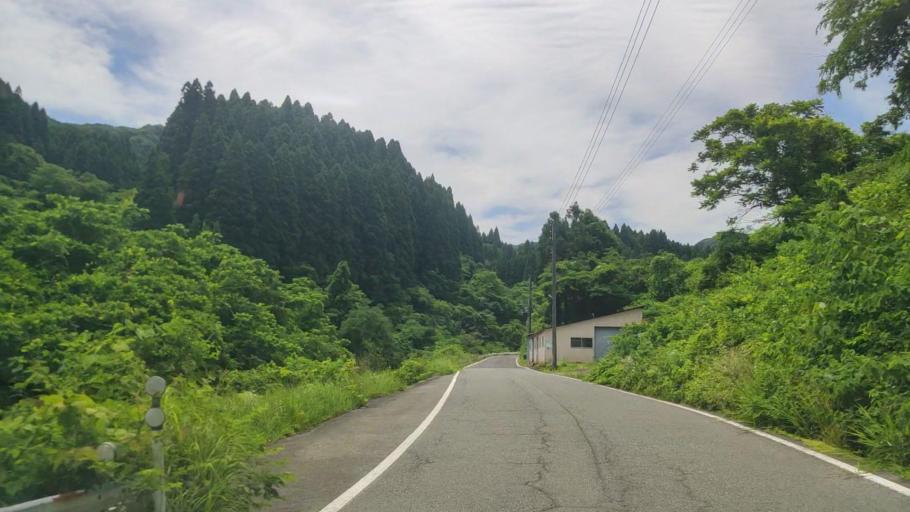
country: JP
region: Tottori
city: Tottori
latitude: 35.4258
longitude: 134.5277
